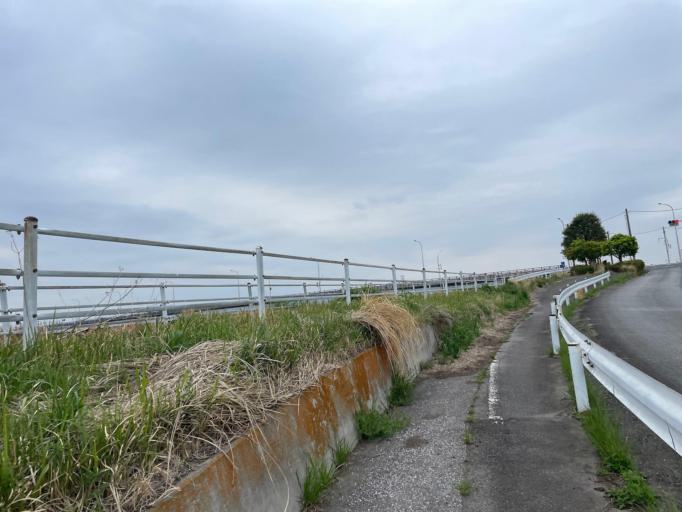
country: JP
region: Gunma
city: Sakai-nakajima
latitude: 36.2735
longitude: 139.2359
